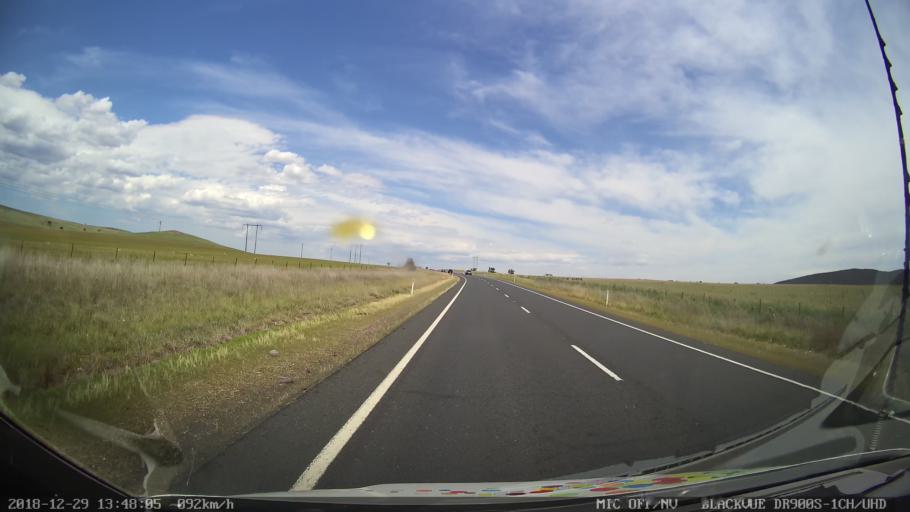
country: AU
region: New South Wales
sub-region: Cooma-Monaro
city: Cooma
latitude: -36.1356
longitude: 149.1458
